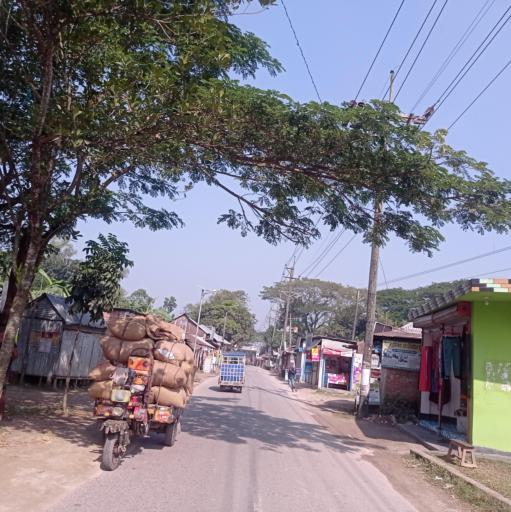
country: BD
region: Dhaka
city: Narsingdi
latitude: 24.0458
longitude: 90.6803
